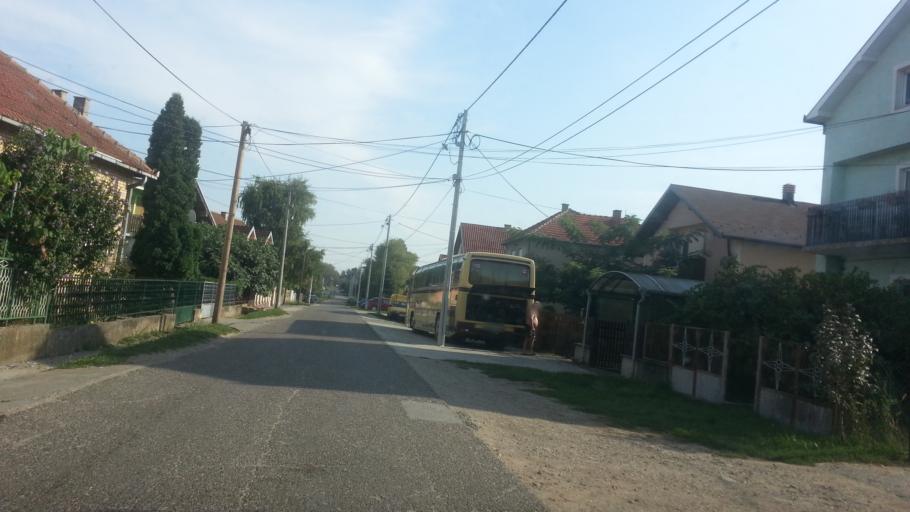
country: RS
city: Novi Banovci
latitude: 44.9582
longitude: 20.2756
